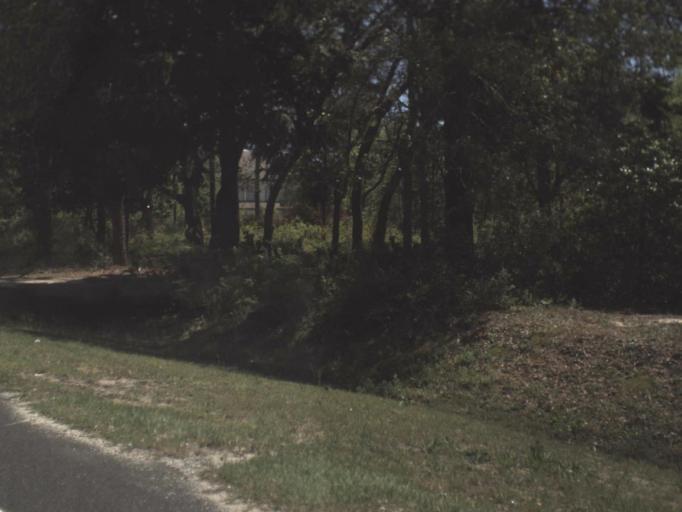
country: US
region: Florida
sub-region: Escambia County
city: Bellview
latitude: 30.4868
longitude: -87.3132
